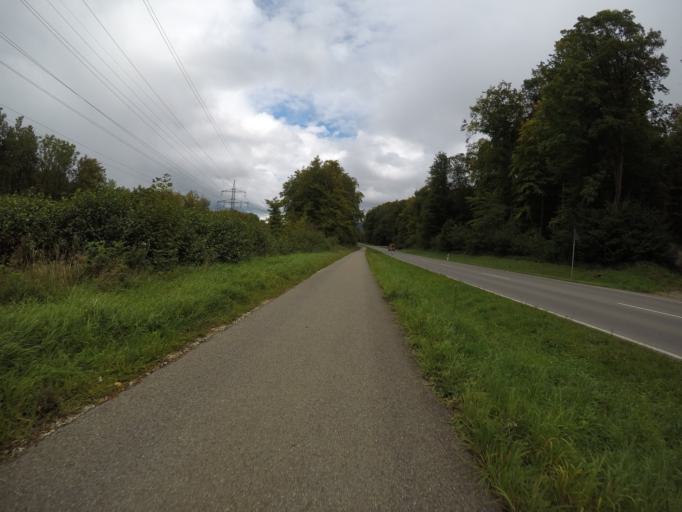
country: DE
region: Baden-Wuerttemberg
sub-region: Tuebingen Region
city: Reutlingen
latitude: 48.4489
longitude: 9.1658
